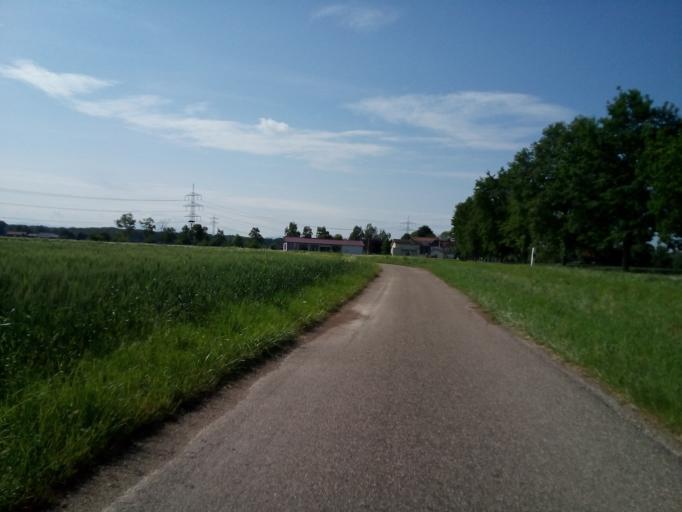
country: DE
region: Baden-Wuerttemberg
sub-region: Freiburg Region
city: Rheinau
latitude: 48.6316
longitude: 7.9212
